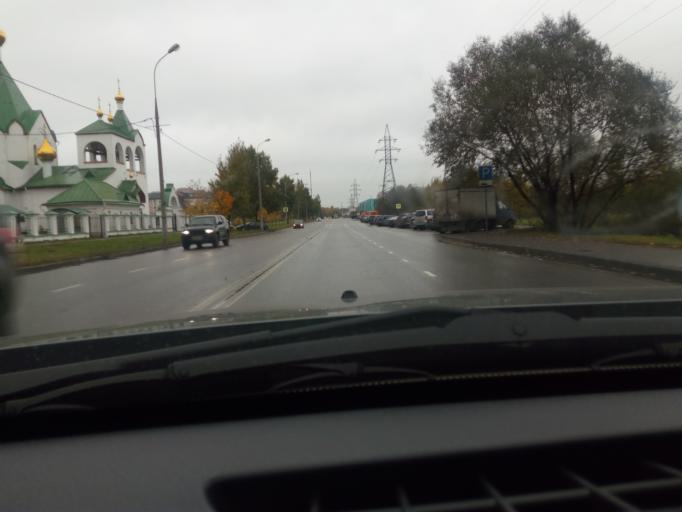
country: RU
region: Moskovskaya
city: Kuskovo
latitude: 55.7361
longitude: 37.8461
